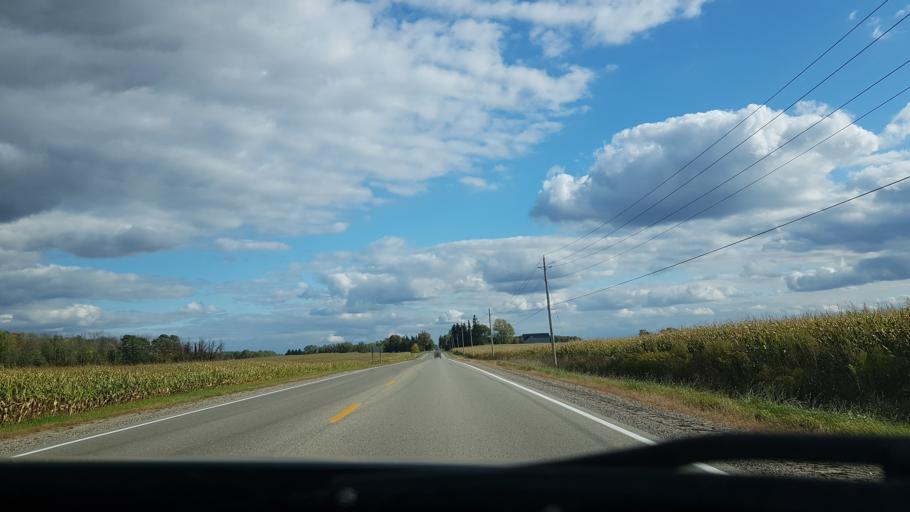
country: CA
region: Ontario
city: Delaware
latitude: 43.0359
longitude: -81.4703
